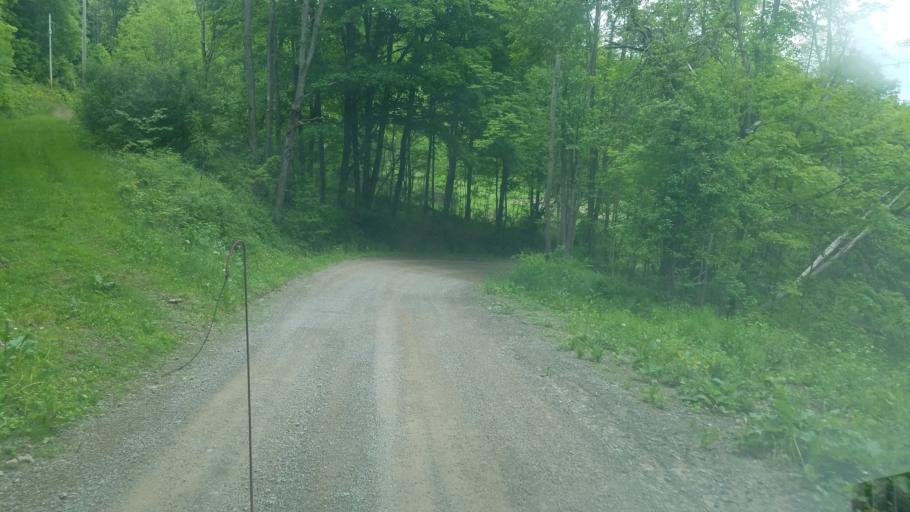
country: US
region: Pennsylvania
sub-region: Tioga County
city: Westfield
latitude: 41.9270
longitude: -77.7081
